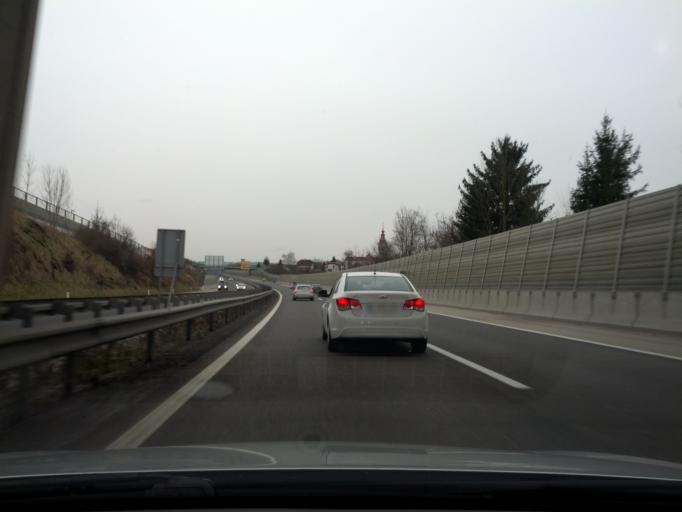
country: SI
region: Grosuplje
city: Smarje-Sap
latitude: 45.9790
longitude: 14.6064
